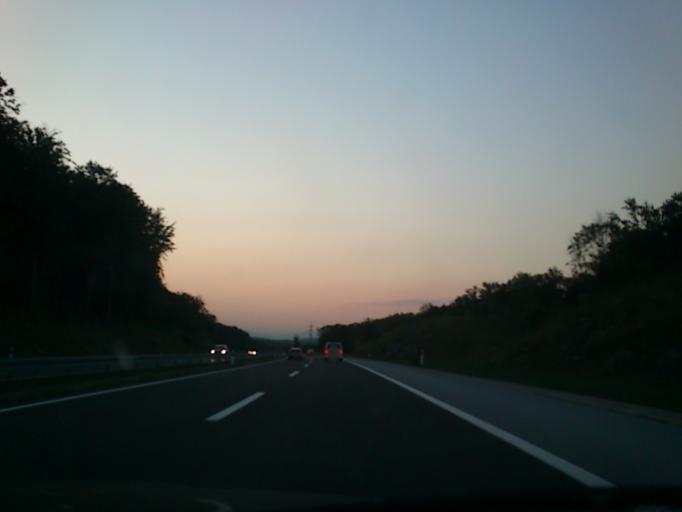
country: HR
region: Karlovacka
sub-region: Grad Ogulin
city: Ogulin
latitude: 45.3589
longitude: 15.2761
